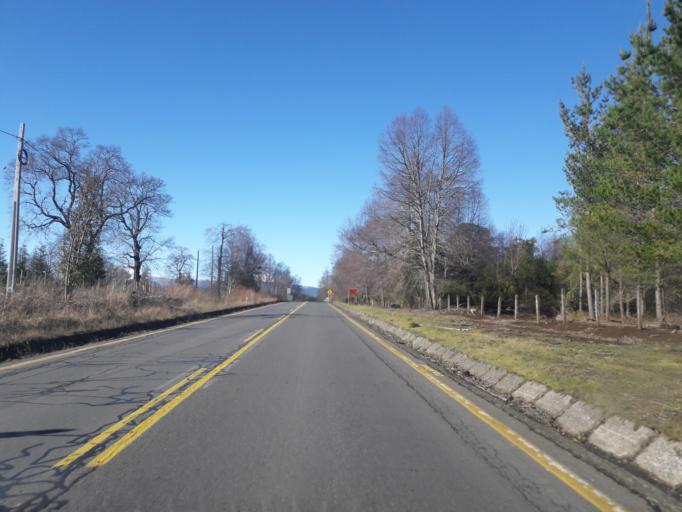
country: CL
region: Araucania
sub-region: Provincia de Malleco
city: Victoria
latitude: -38.3292
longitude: -71.9867
